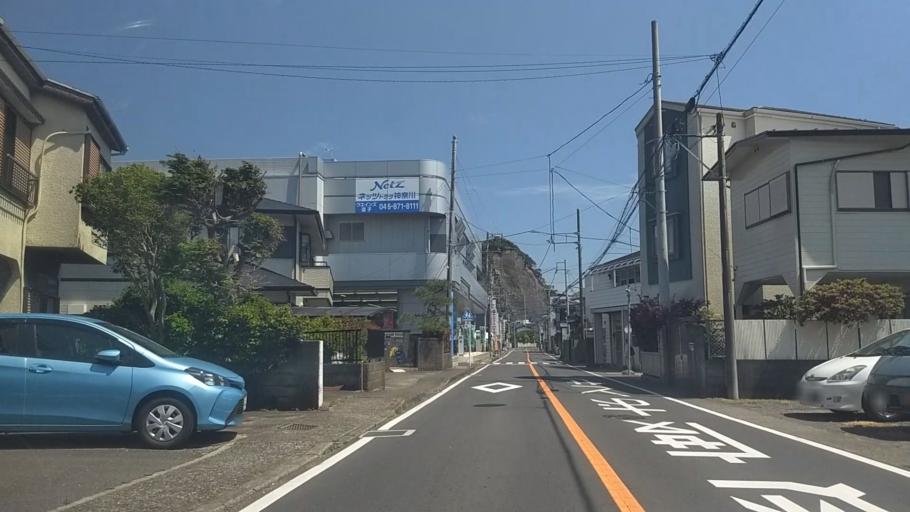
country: JP
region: Kanagawa
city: Zushi
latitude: 35.3007
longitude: 139.5717
